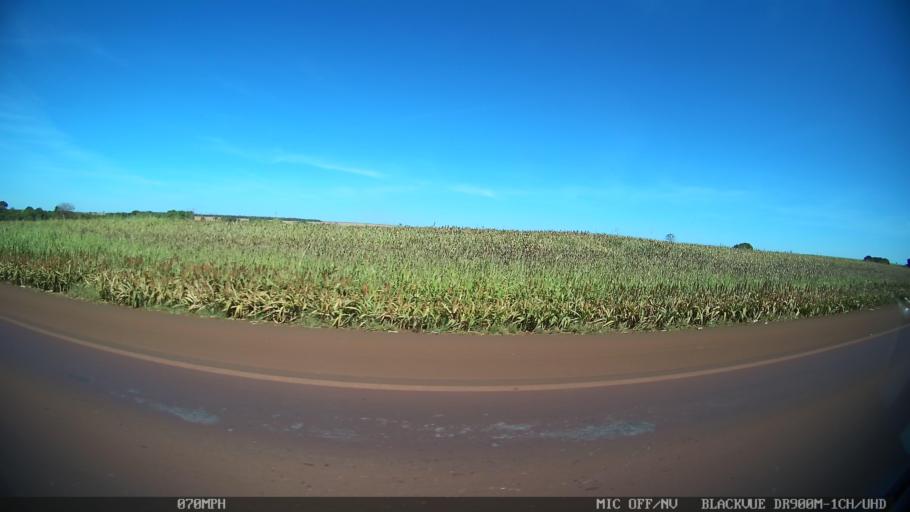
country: BR
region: Sao Paulo
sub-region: Ipua
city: Ipua
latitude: -20.4922
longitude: -47.9914
